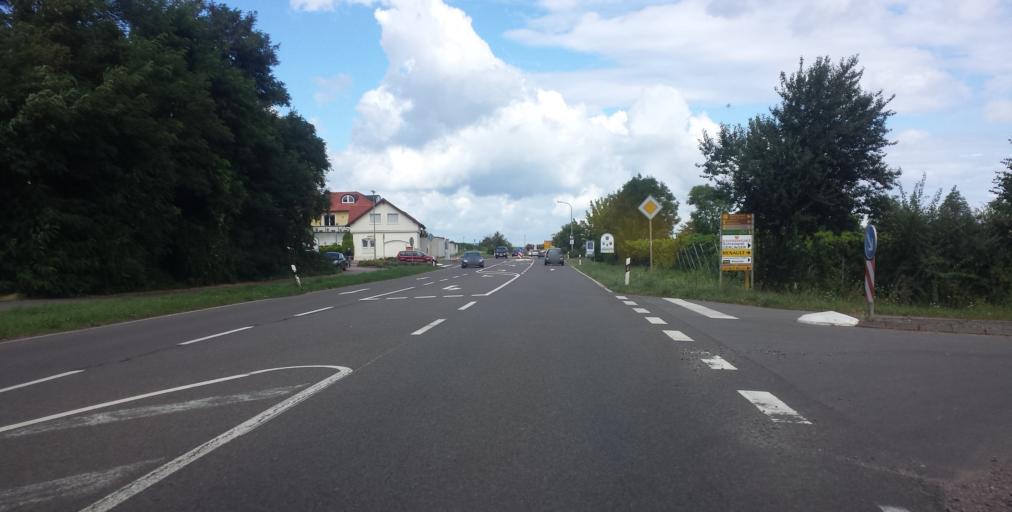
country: DE
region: Rheinland-Pfalz
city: Maikammer
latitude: 49.3029
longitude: 8.1416
